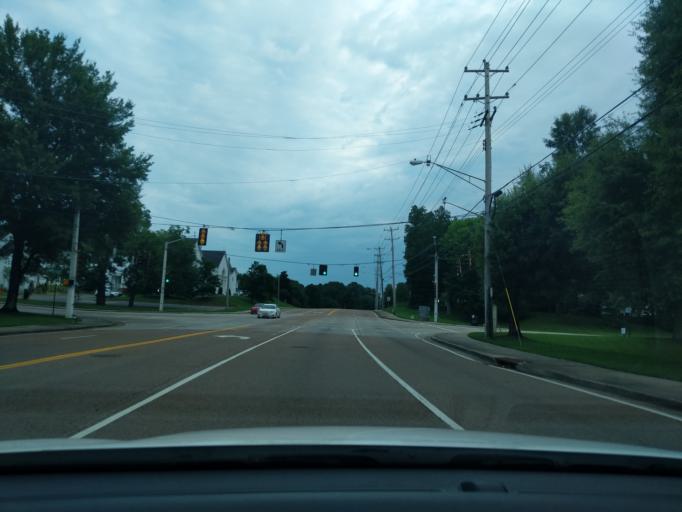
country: US
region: Tennessee
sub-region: Shelby County
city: Germantown
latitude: 35.0856
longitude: -89.8114
